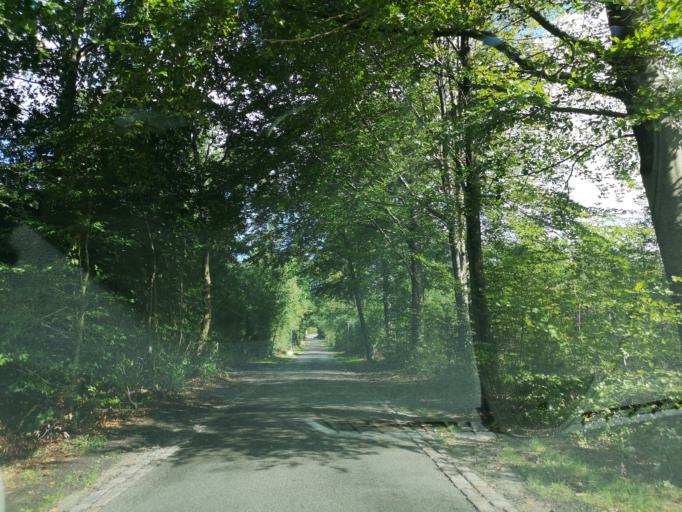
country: DK
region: Central Jutland
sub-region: Holstebro Kommune
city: Holstebro
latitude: 56.3378
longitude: 8.6324
